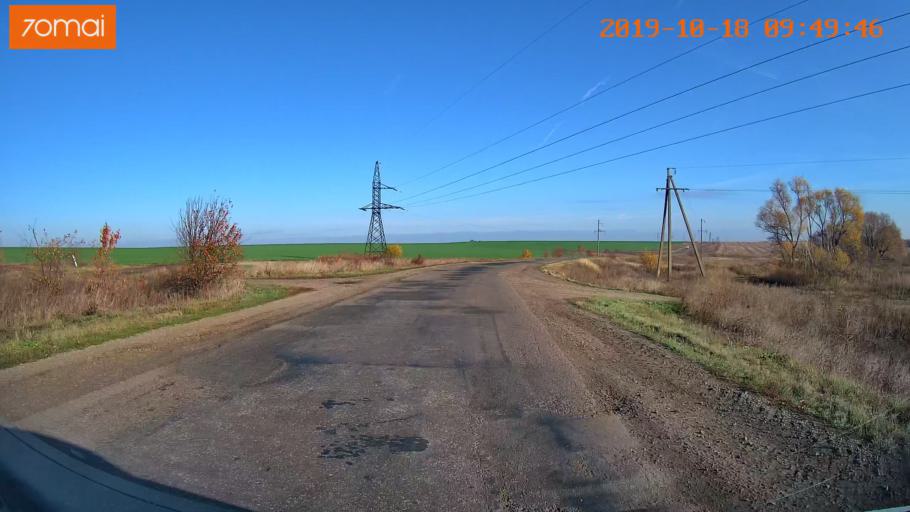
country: RU
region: Tula
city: Kazachka
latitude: 53.3215
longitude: 38.2691
